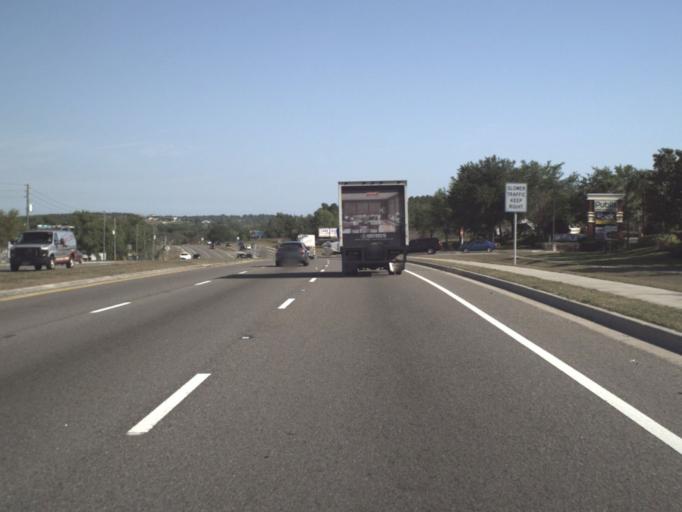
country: US
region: Florida
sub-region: Lake County
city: Minneola
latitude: 28.5654
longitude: -81.7441
